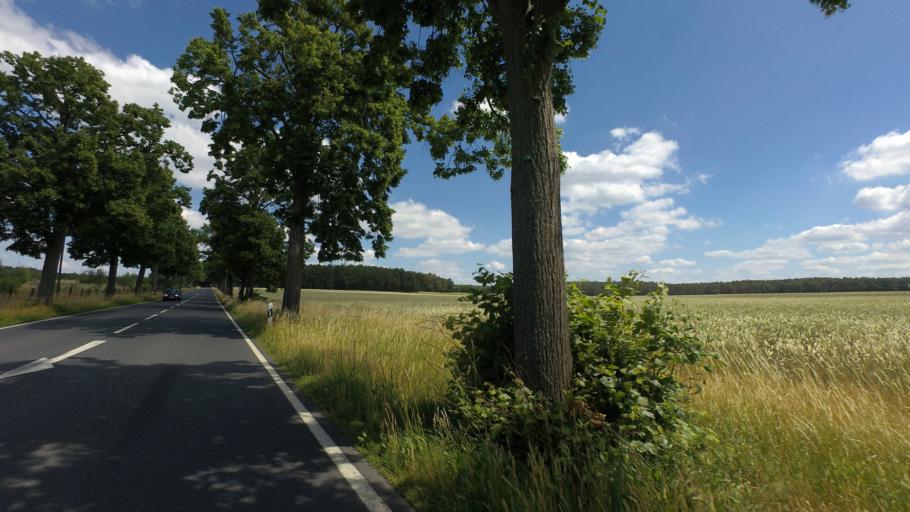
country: DE
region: Brandenburg
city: Sonnewalde
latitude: 51.7150
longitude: 13.6697
